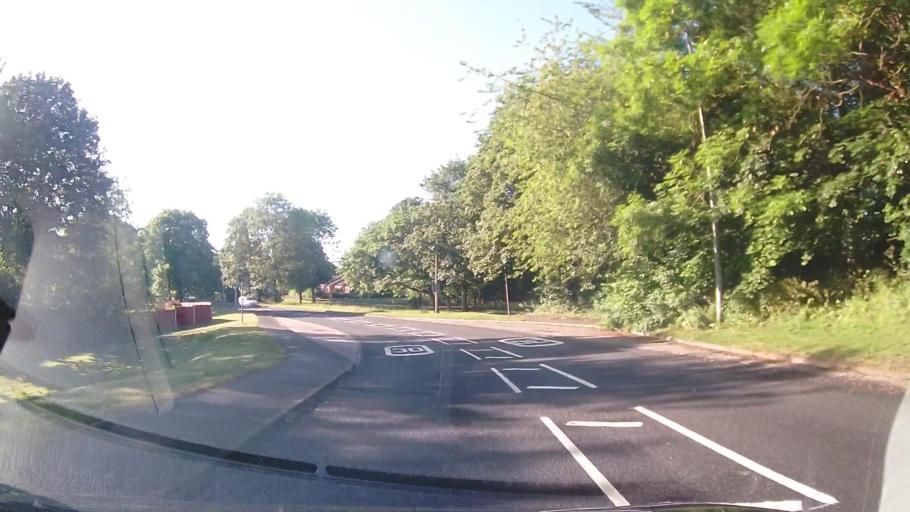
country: GB
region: England
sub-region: Shropshire
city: Hadley
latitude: 52.7078
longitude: -2.4925
